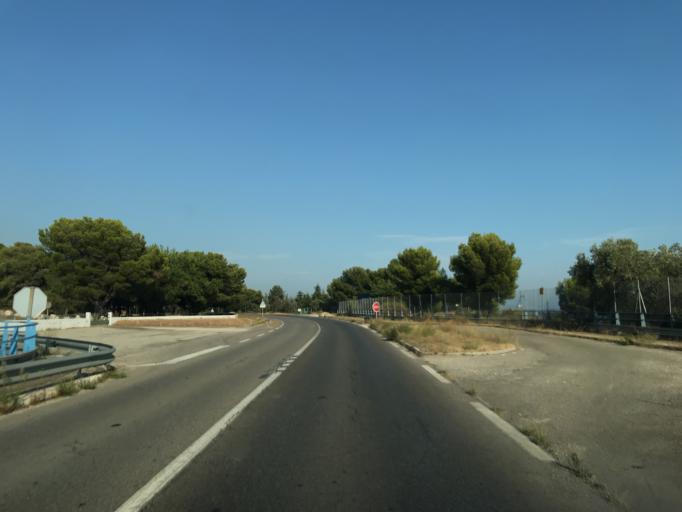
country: FR
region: Provence-Alpes-Cote d'Azur
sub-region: Departement des Bouches-du-Rhone
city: Cornillon-Confoux
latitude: 43.5268
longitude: 5.0735
